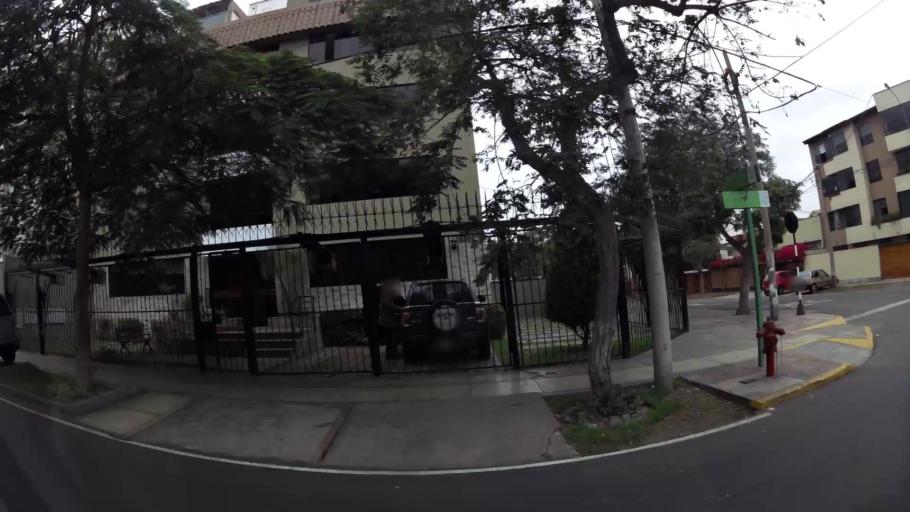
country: PE
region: Lima
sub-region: Lima
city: Surco
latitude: -12.1206
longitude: -77.0158
